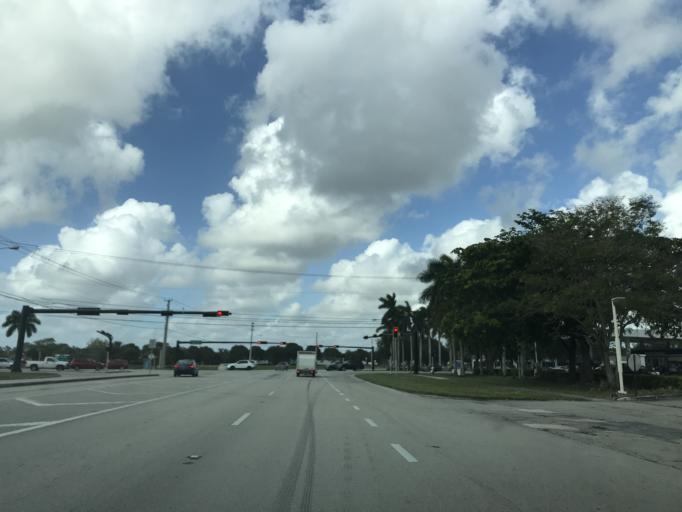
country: US
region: Florida
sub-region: Broward County
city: Margate
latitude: 26.2547
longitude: -80.1947
